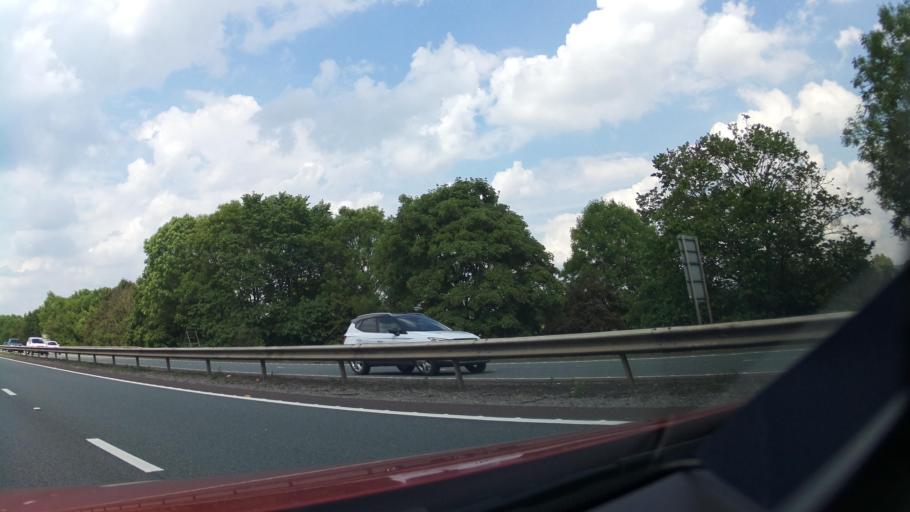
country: GB
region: England
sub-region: North Yorkshire
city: Thirsk
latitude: 54.2507
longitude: -1.3430
